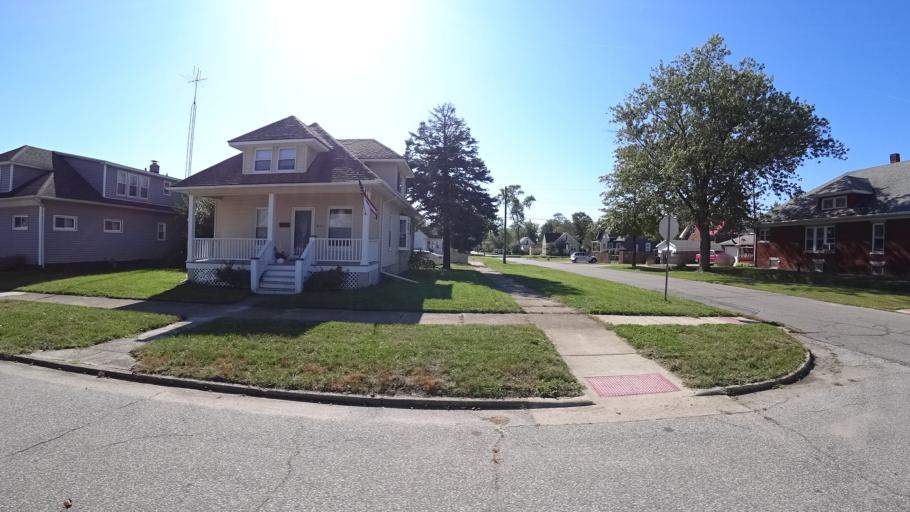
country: US
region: Indiana
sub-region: LaPorte County
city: Michigan City
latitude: 41.7107
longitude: -86.8906
